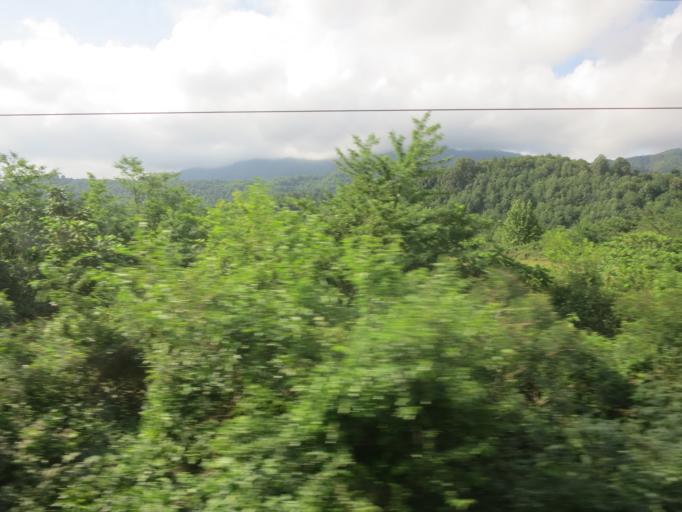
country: GE
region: Samegrelo and Zemo Svaneti
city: Abasha
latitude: 42.0949
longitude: 42.2235
